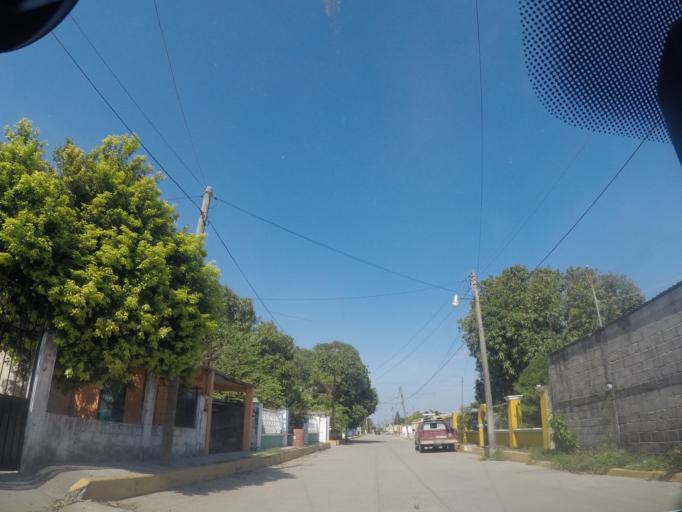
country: MX
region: Oaxaca
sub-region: Salina Cruz
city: Salina Cruz
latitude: 16.2169
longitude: -95.1958
